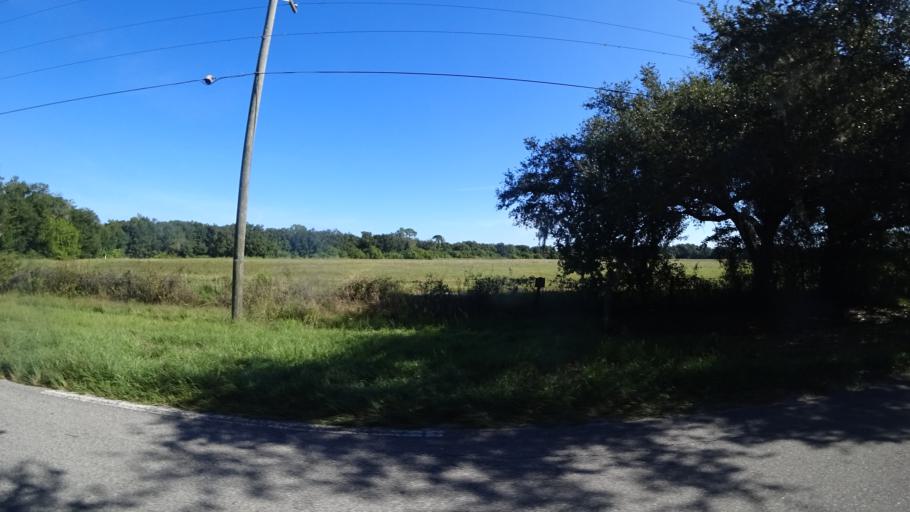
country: US
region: Florida
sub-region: Hillsborough County
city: Sun City Center
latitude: 27.6657
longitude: -82.3347
